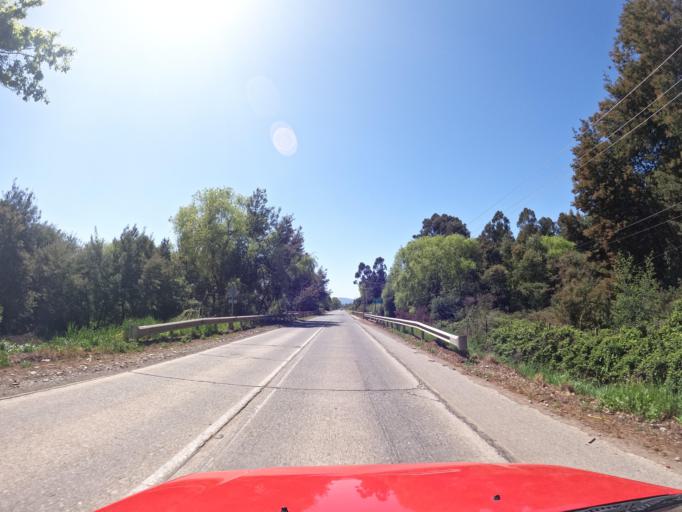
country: CL
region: Maule
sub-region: Provincia de Linares
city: Colbun
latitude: -35.7742
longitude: -71.4306
